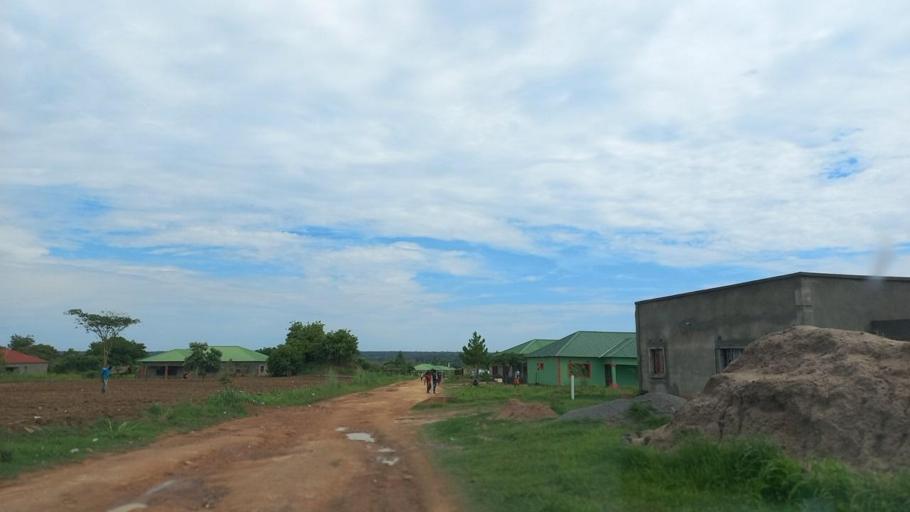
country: ZM
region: Copperbelt
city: Kitwe
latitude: -12.8721
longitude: 28.3340
